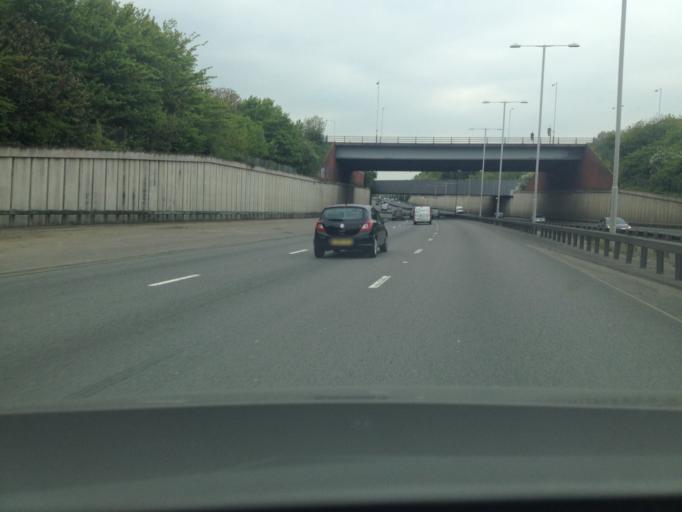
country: GB
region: England
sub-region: Greater London
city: Ruislip
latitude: 51.5536
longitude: -0.4458
